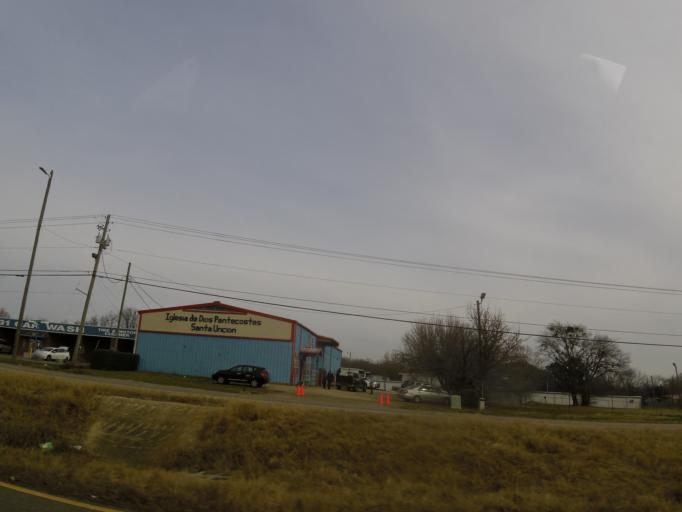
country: US
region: Alabama
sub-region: Montgomery County
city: Montgomery
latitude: 32.3179
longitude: -86.2322
